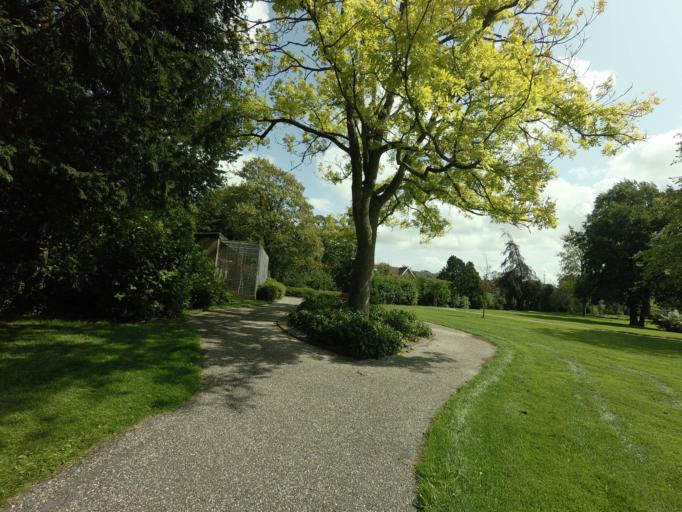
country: NL
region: Friesland
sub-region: Gemeente Franekeradeel
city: Franeker
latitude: 53.1862
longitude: 5.5359
